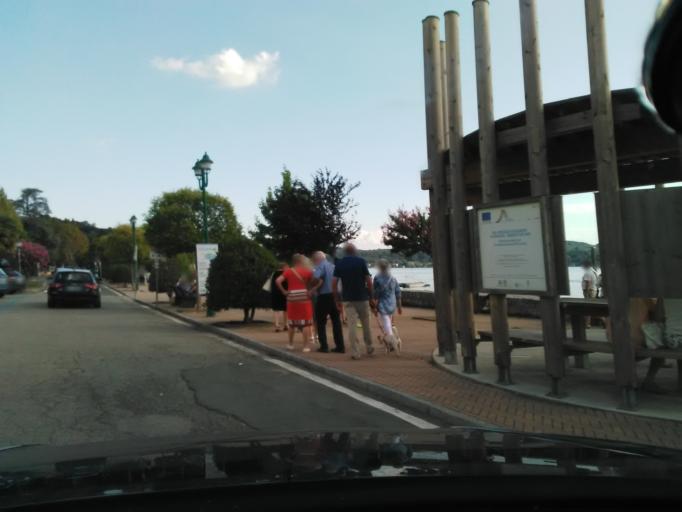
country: IT
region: Piedmont
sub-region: Provincia di Biella
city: Viverone
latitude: 45.4221
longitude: 8.0456
